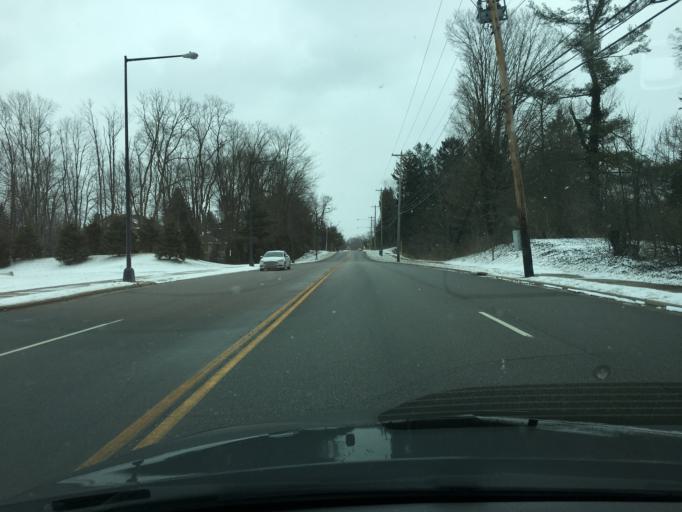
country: US
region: Ohio
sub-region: Summit County
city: Fairlawn
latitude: 41.1359
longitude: -81.6125
